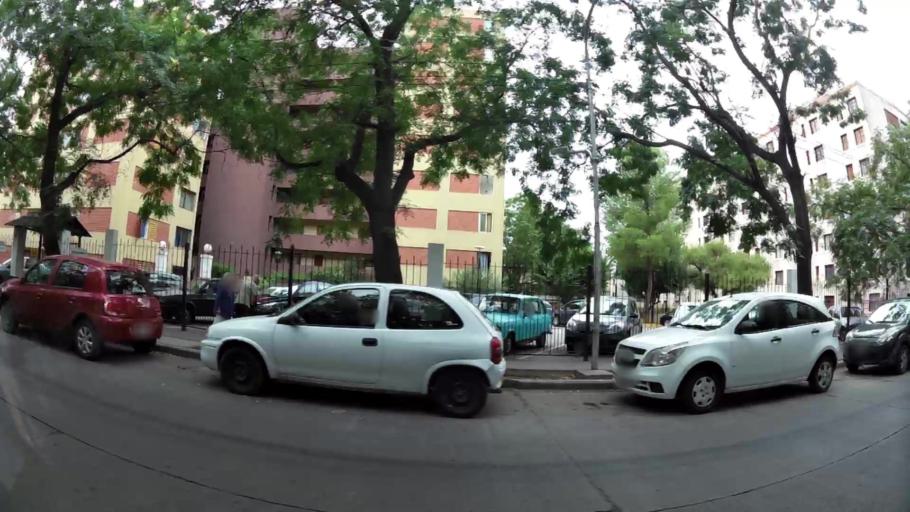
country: AR
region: Mendoza
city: Mendoza
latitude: -32.8741
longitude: -68.8443
